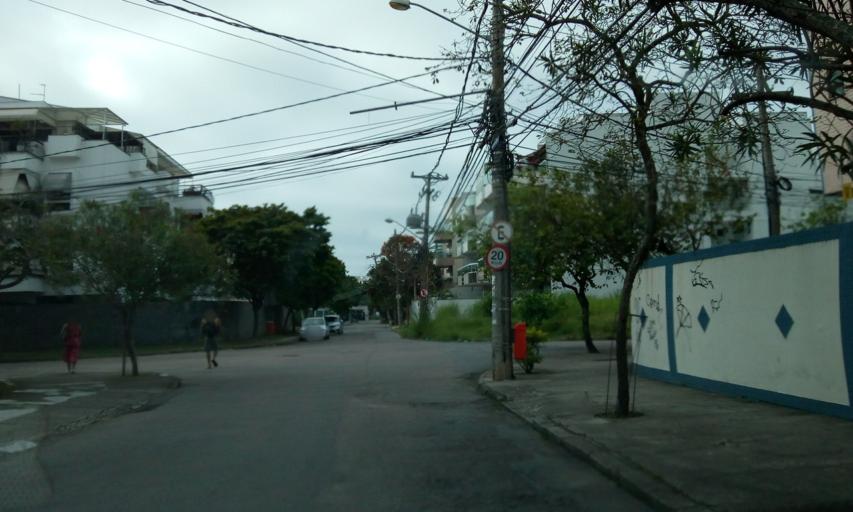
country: BR
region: Rio de Janeiro
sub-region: Nilopolis
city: Nilopolis
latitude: -23.0132
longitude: -43.4532
